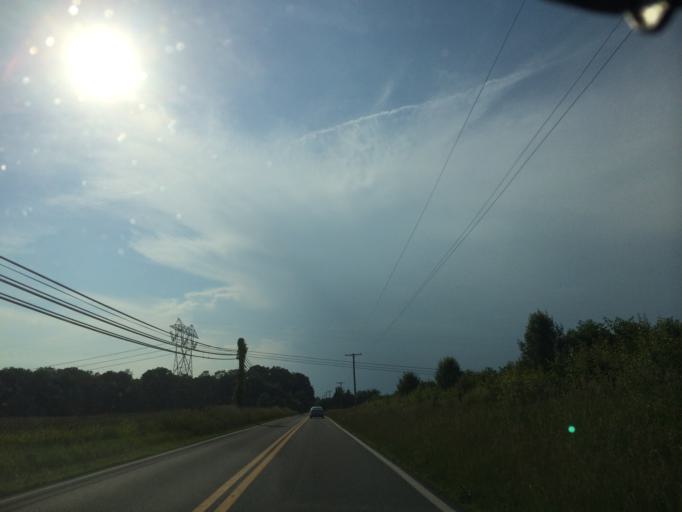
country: US
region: Maryland
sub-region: Carroll County
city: Sykesville
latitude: 39.4098
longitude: -77.0220
